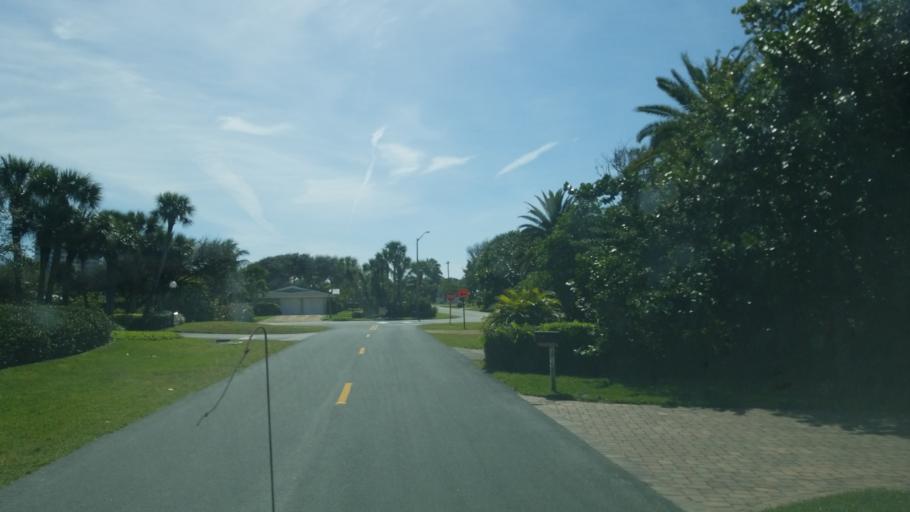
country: US
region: Florida
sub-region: Indian River County
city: Vero Beach
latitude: 27.6602
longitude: -80.3594
